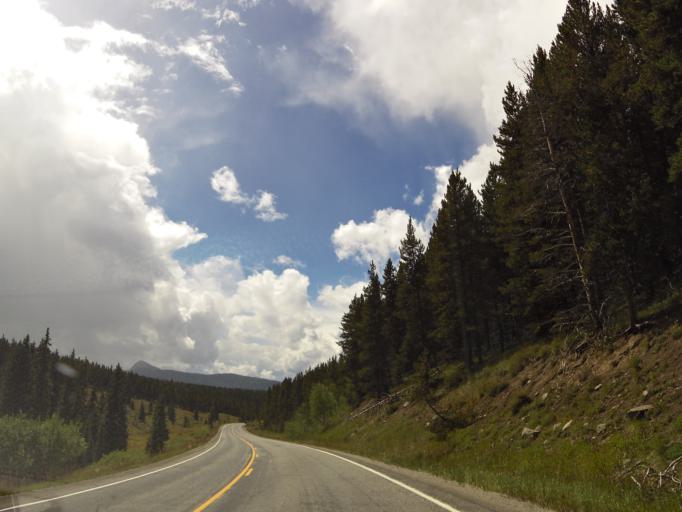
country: US
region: Colorado
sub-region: San Juan County
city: Silverton
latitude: 37.7349
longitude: -107.7160
